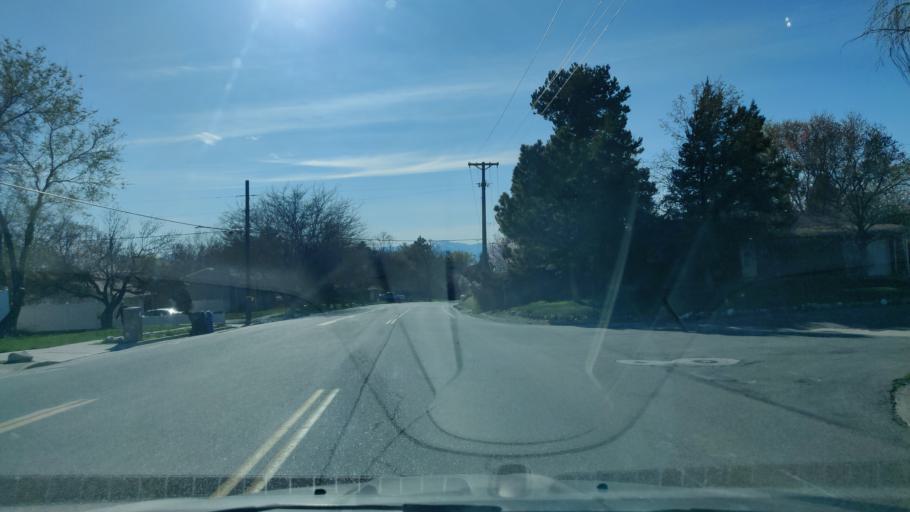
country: US
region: Utah
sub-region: Salt Lake County
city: Cottonwood Heights
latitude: 40.6094
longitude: -111.8144
